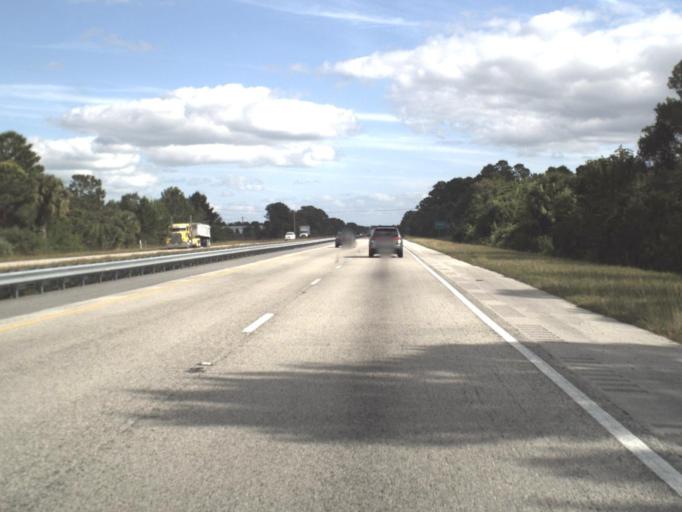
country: US
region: Florida
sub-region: Brevard County
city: Sharpes
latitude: 28.4057
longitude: -80.7832
